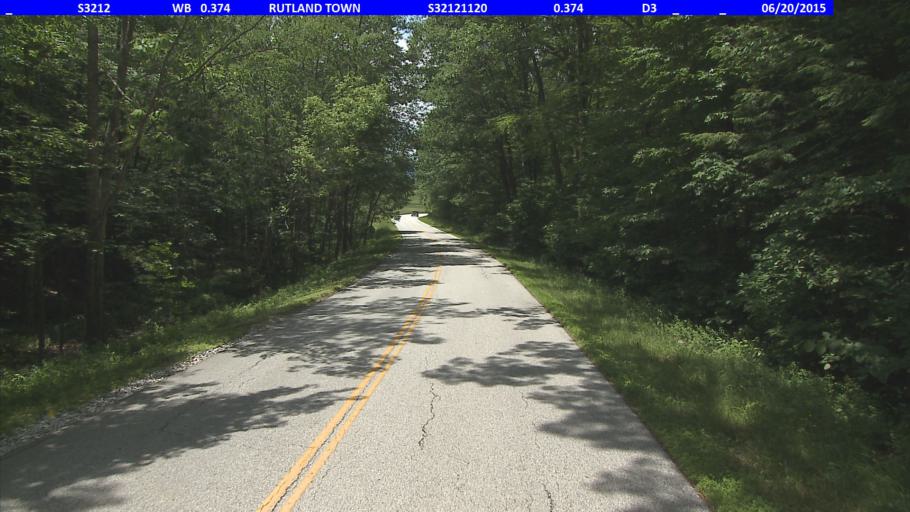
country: US
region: Vermont
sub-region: Rutland County
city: Rutland
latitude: 43.6453
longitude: -72.9401
